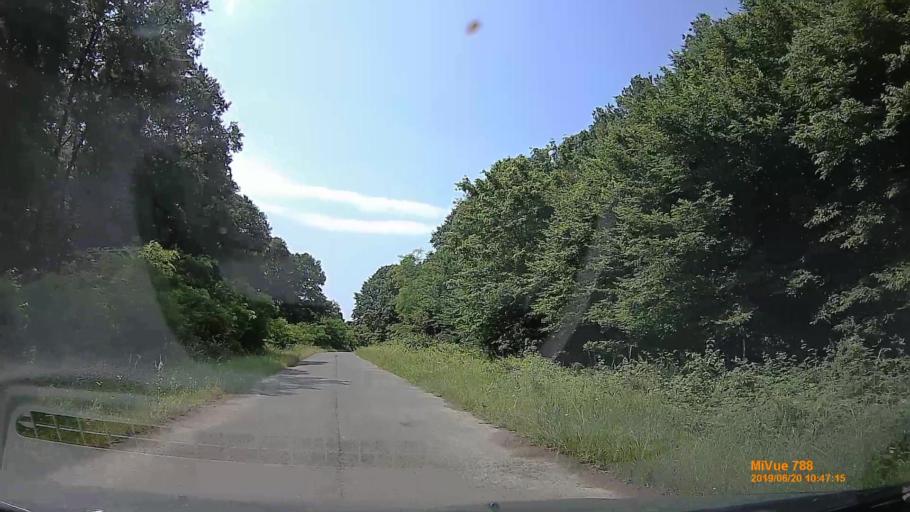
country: HU
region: Baranya
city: Hidas
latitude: 46.1764
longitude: 18.5820
